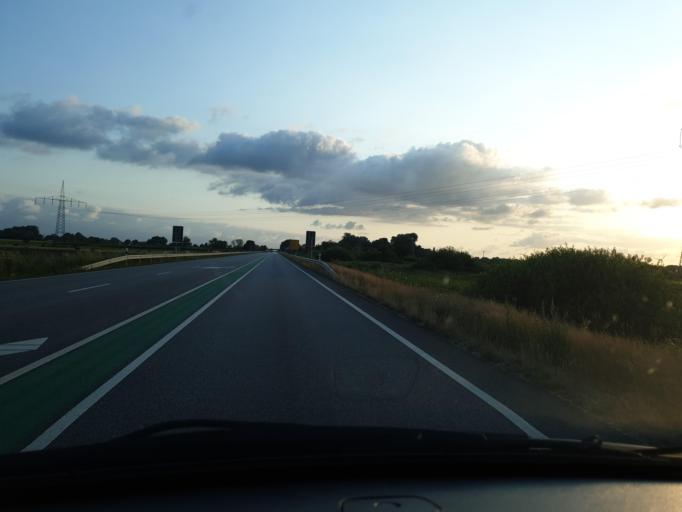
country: DE
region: Schleswig-Holstein
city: Bekmunde
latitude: 53.9379
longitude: 9.4439
